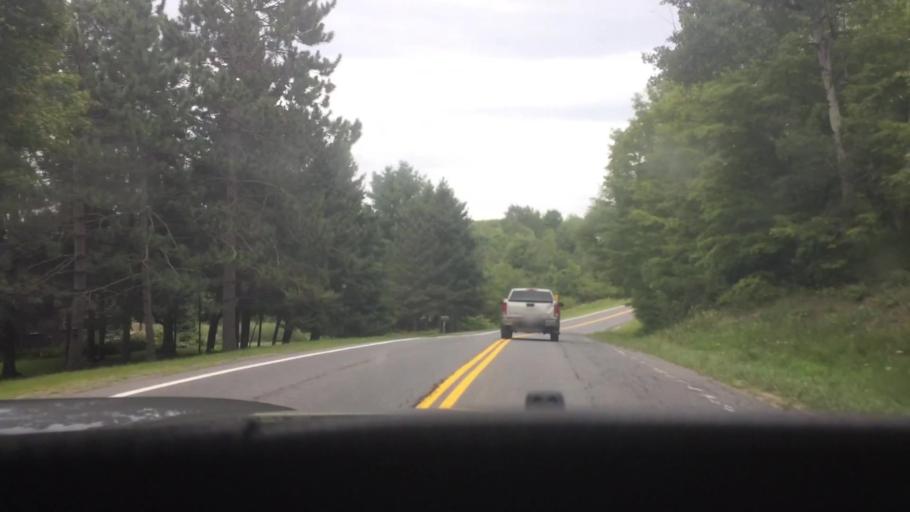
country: US
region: New York
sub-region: St. Lawrence County
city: Canton
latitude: 44.5345
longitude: -75.1761
